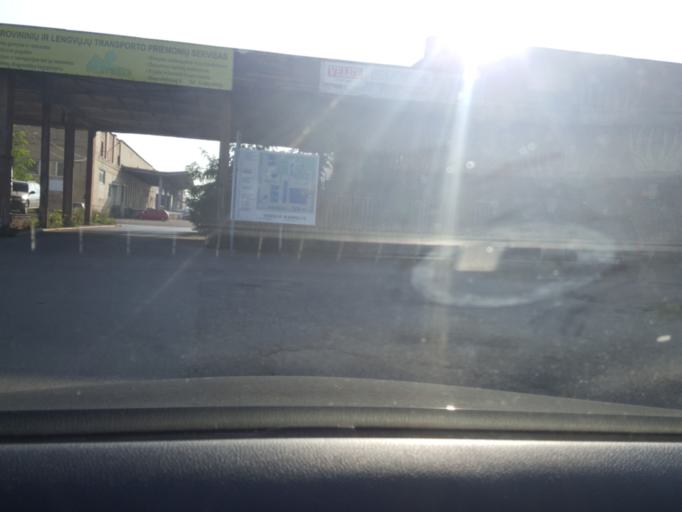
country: LT
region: Alytaus apskritis
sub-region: Alytus
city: Alytus
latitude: 54.4334
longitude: 24.0194
